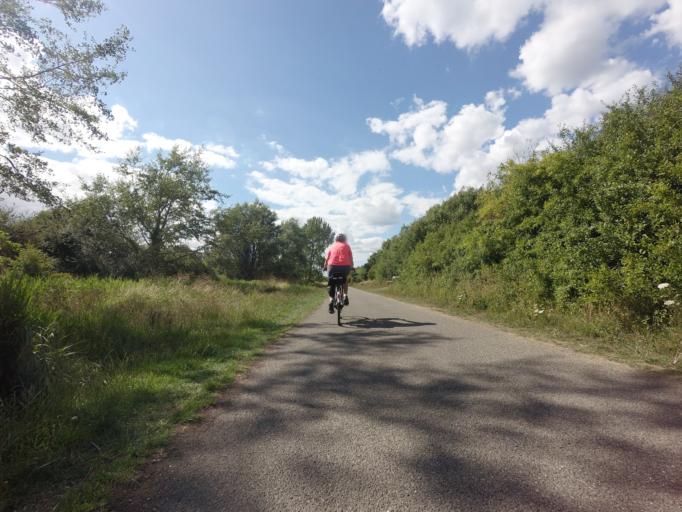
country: GB
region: England
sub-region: East Sussex
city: Eastbourne
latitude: 50.8034
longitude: 0.2876
